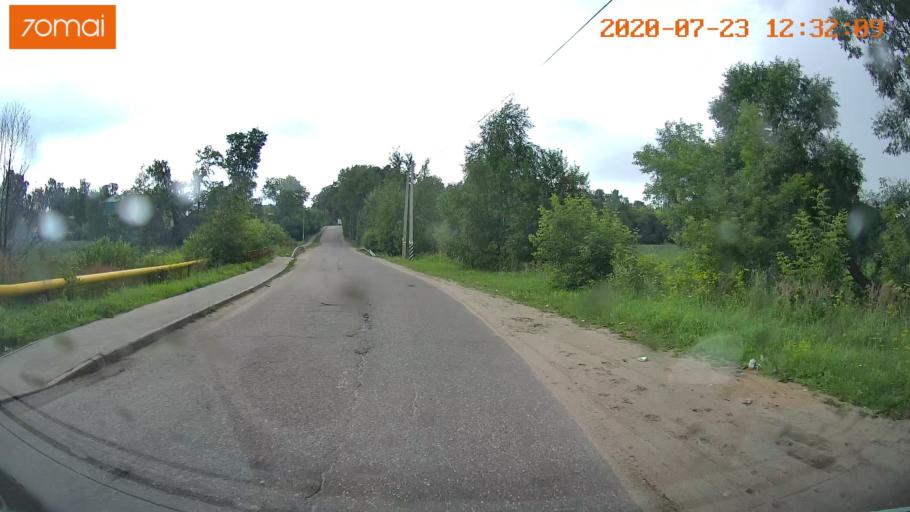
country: RU
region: Ivanovo
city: Bogorodskoye
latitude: 57.0458
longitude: 41.0102
